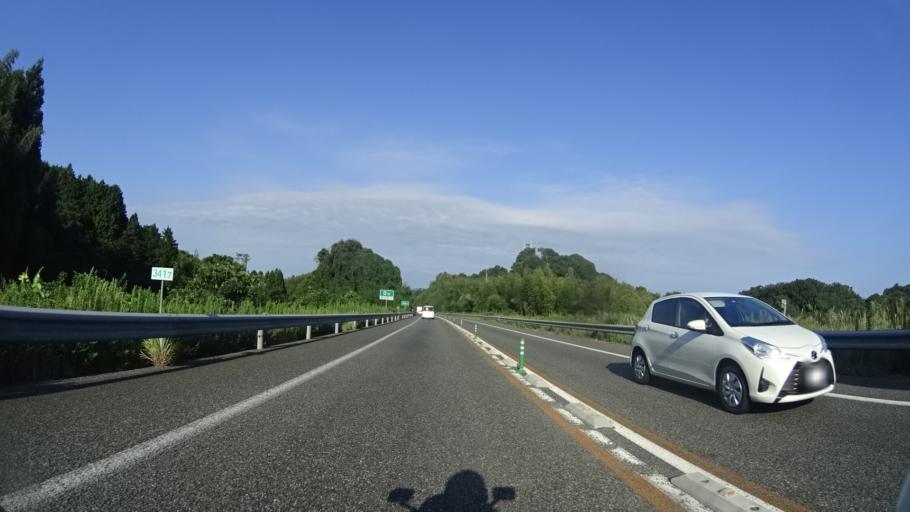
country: JP
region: Shimane
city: Matsue-shi
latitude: 35.4119
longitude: 132.9595
